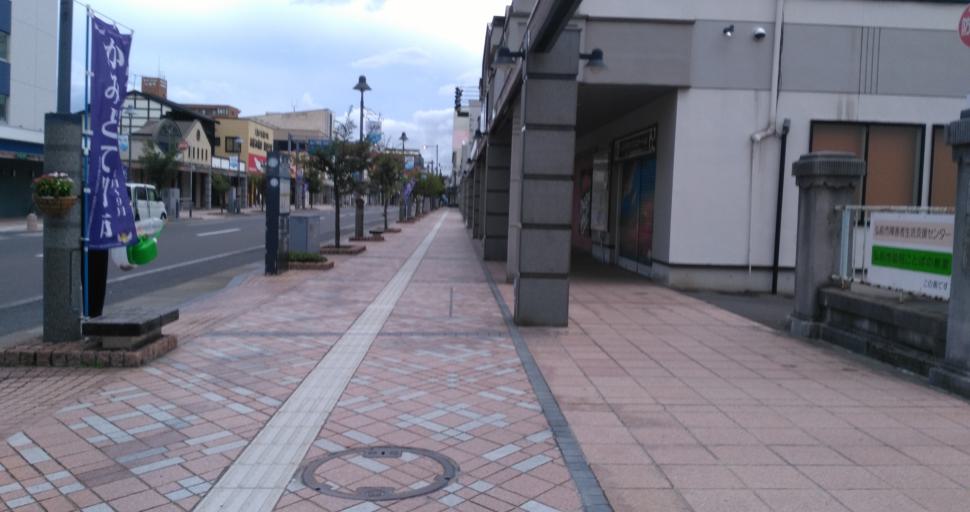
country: JP
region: Aomori
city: Hirosaki
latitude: 40.5975
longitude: 140.4767
